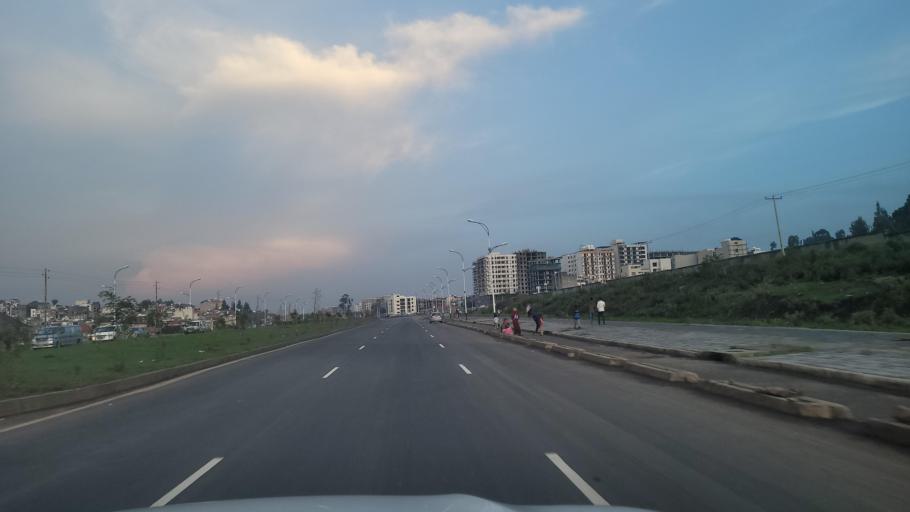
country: ET
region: Adis Abeba
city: Addis Ababa
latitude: 8.9441
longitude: 38.7177
